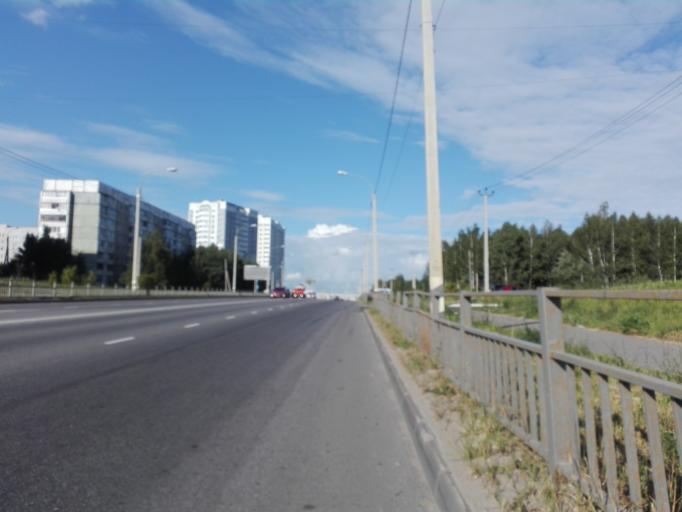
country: RU
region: Orjol
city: Orel
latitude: 53.0026
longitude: 36.1095
